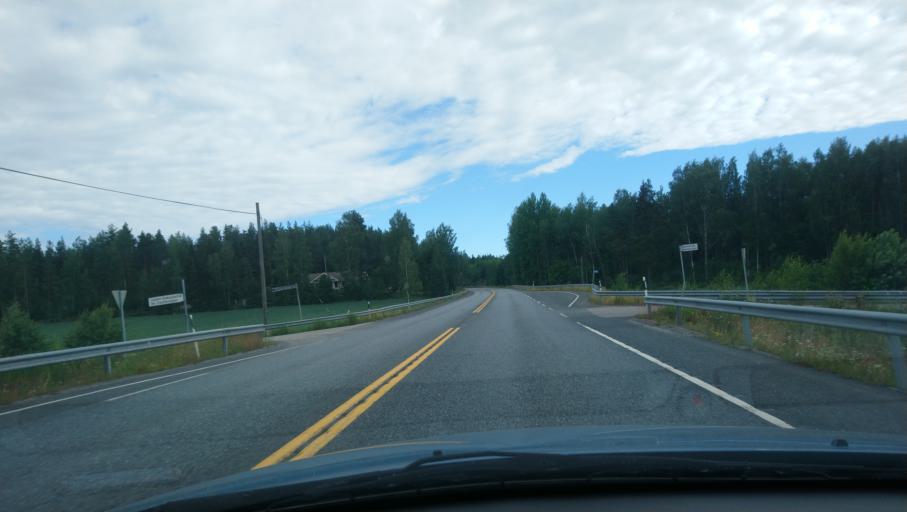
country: FI
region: Uusimaa
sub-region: Porvoo
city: Porvoo
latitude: 60.4221
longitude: 25.5793
